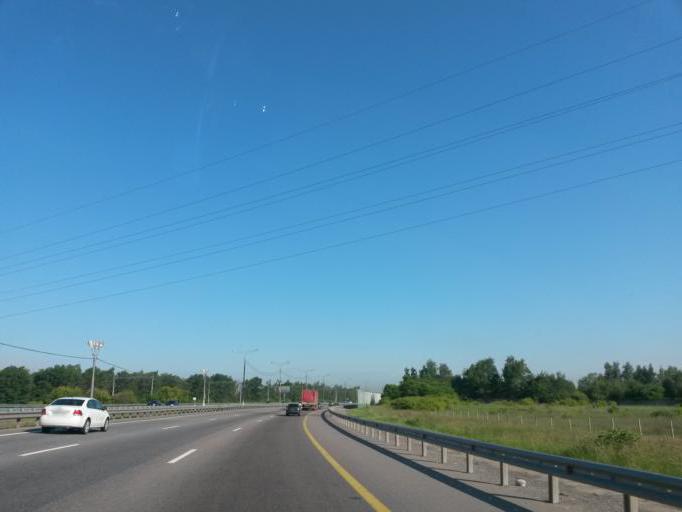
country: RU
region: Moskovskaya
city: Domodedovo
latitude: 55.4629
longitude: 37.7590
